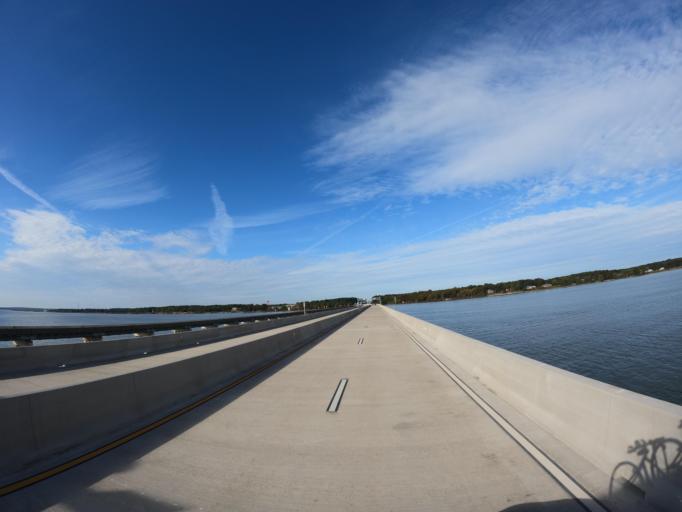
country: US
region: Virginia
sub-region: King George County
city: Dahlgren
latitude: 38.3602
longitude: -77.0038
